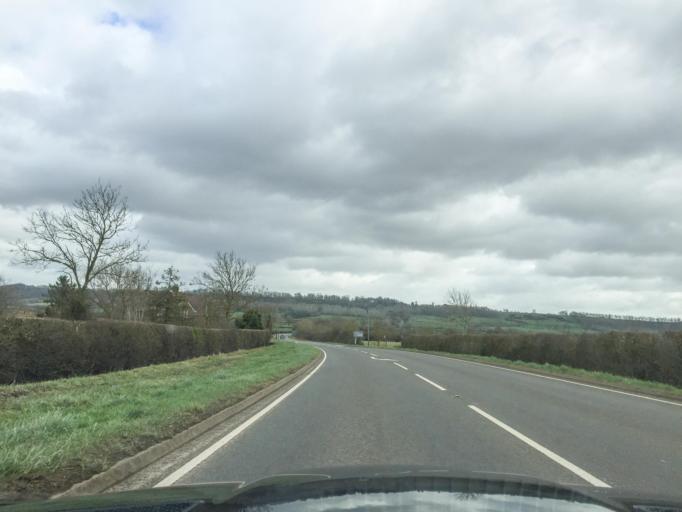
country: GB
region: England
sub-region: Warwickshire
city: Wellesbourne Mountford
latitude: 52.1200
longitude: -1.5036
